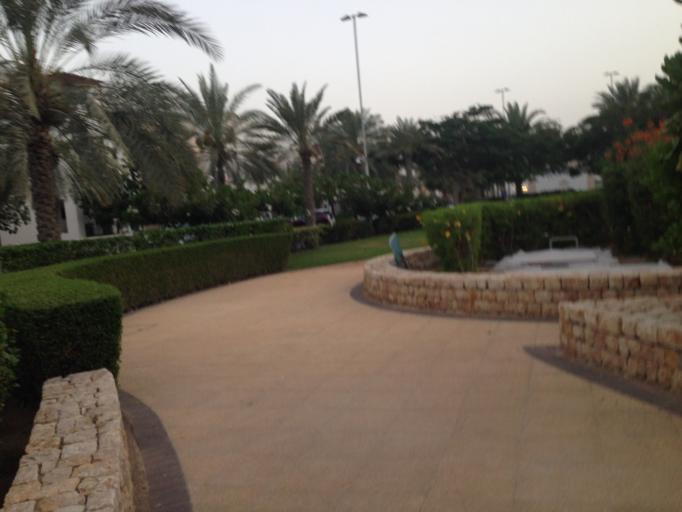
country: OM
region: Muhafazat Masqat
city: As Sib al Jadidah
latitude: 23.6268
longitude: 58.2650
